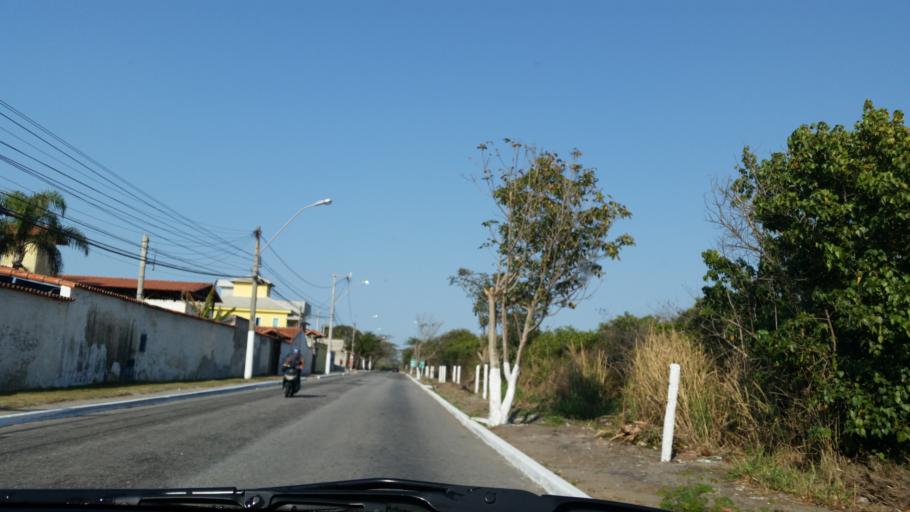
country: BR
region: Rio de Janeiro
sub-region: Cabo Frio
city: Cabo Frio
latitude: -22.8643
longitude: -41.9994
